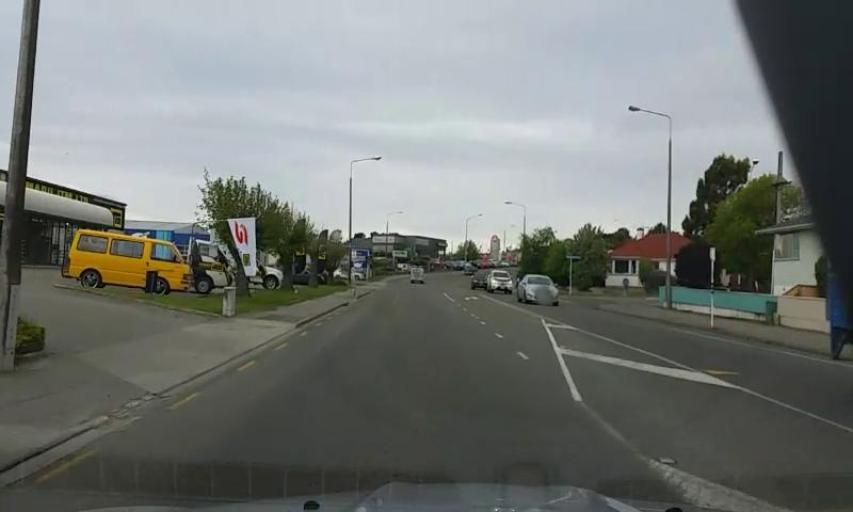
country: NZ
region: Canterbury
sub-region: Timaru District
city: Timaru
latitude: -44.3745
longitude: 171.2422
